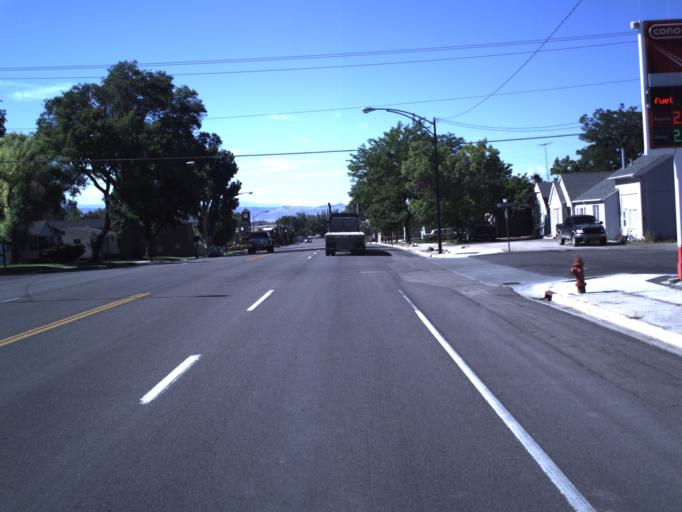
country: US
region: Utah
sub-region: Sanpete County
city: Gunnison
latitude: 39.1570
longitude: -111.8183
